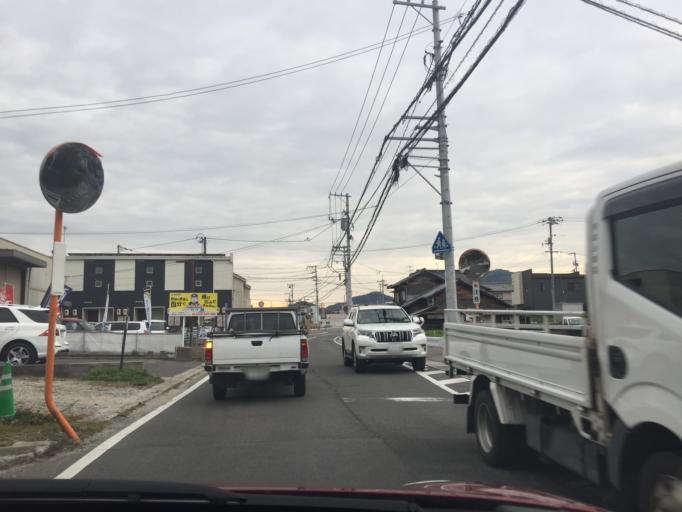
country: JP
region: Hiroshima
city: Hiroshima-shi
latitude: 34.4509
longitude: 132.4642
